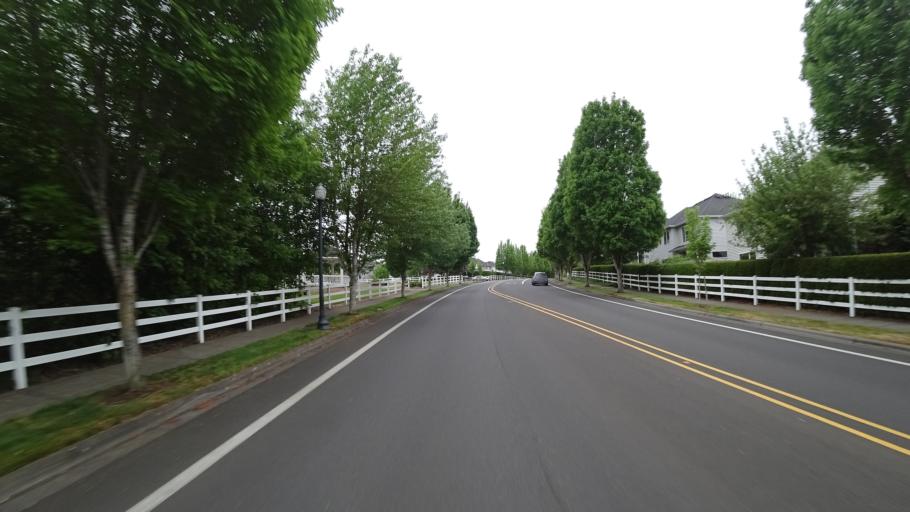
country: US
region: Oregon
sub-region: Washington County
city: Bethany
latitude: 45.5512
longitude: -122.8542
